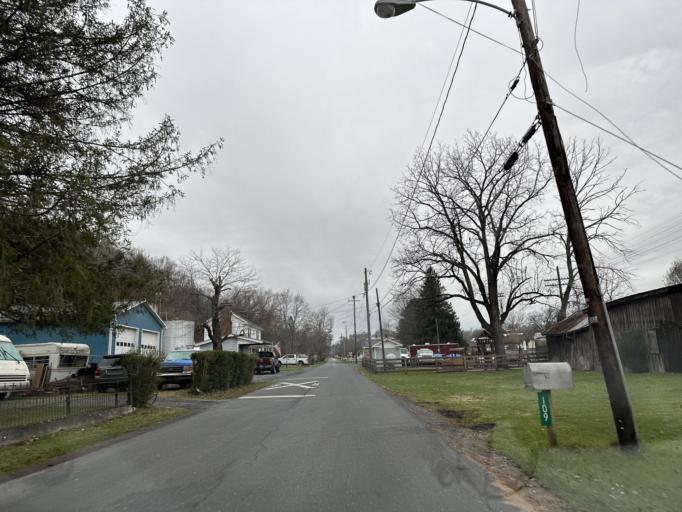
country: US
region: Virginia
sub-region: Rockbridge County
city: East Lexington
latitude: 38.0770
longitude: -79.3843
